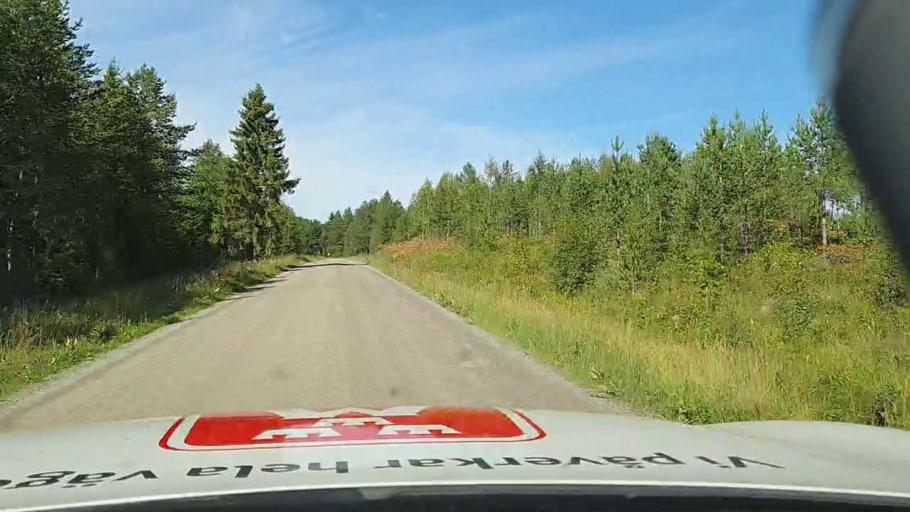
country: SE
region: Jaemtland
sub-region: Stroemsunds Kommun
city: Stroemsund
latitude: 63.6893
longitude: 15.3849
